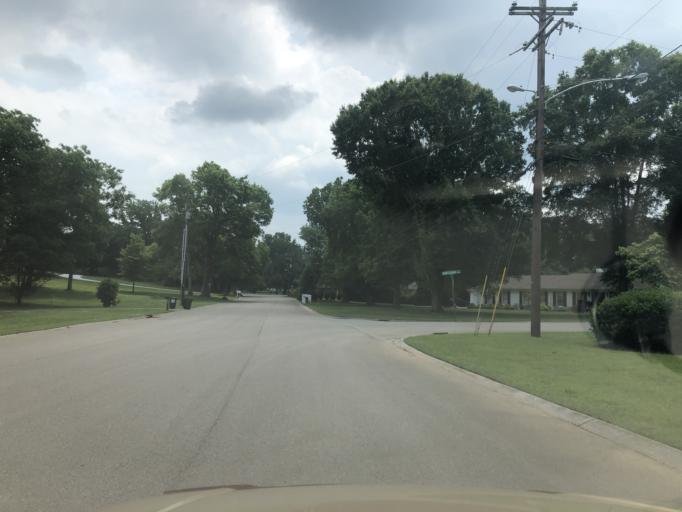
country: US
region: Tennessee
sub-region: Davidson County
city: Lakewood
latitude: 36.2346
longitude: -86.6163
